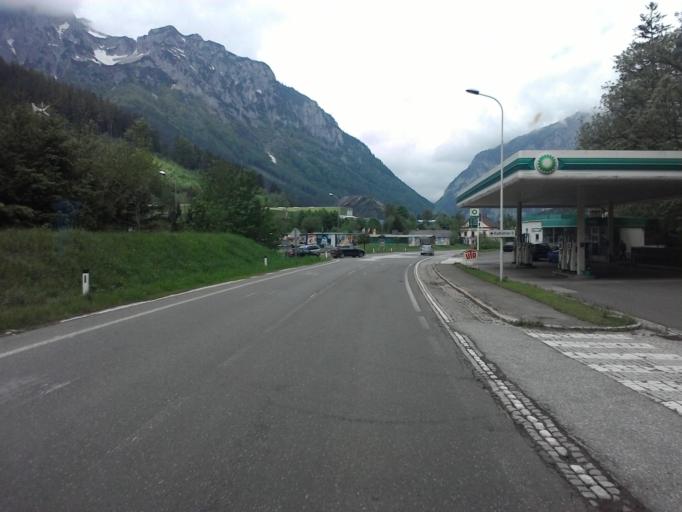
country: AT
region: Styria
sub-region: Politischer Bezirk Leoben
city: Eisenerz
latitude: 47.5518
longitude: 14.8749
